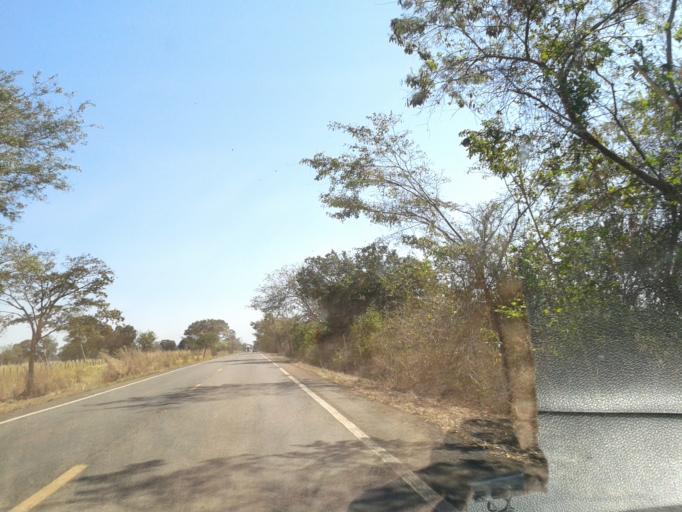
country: BR
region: Goias
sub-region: Sao Miguel Do Araguaia
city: Sao Miguel do Araguaia
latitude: -13.9223
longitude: -50.3224
